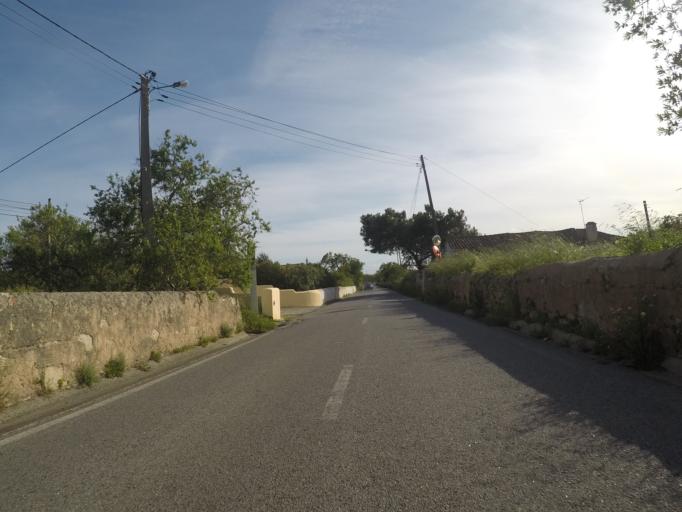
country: PT
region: Faro
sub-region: Lagos
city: Lagos
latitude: 37.1043
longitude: -8.7109
